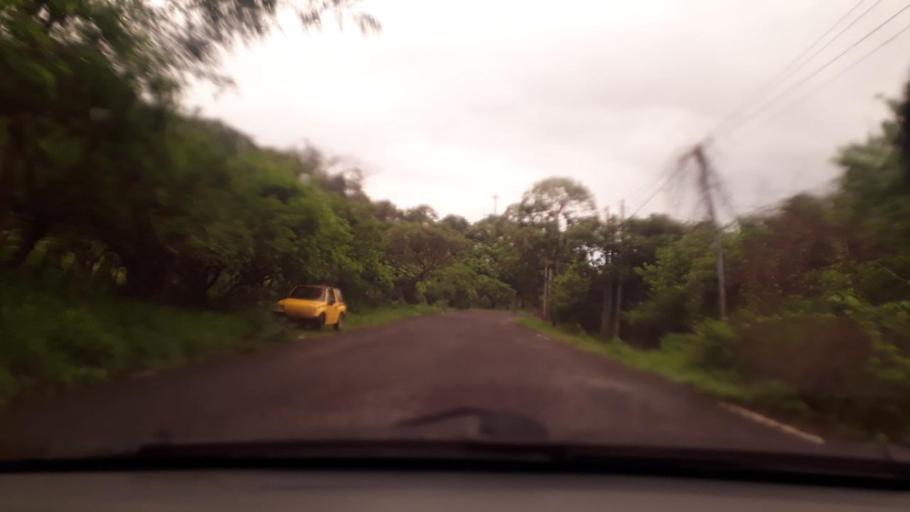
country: GT
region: Jutiapa
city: Comapa
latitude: 14.0399
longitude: -89.9161
